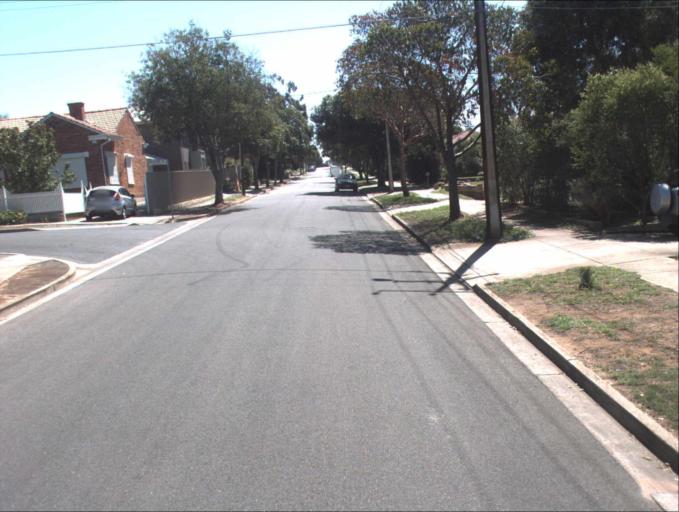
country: AU
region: South Australia
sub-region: Port Adelaide Enfield
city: Klemzig
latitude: -34.8826
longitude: 138.6301
